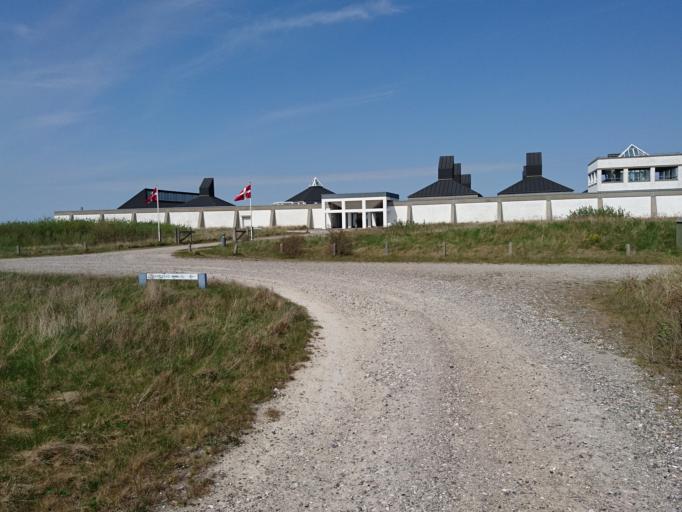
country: DK
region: North Denmark
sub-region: Frederikshavn Kommune
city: Skagen
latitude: 57.7391
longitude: 10.5960
